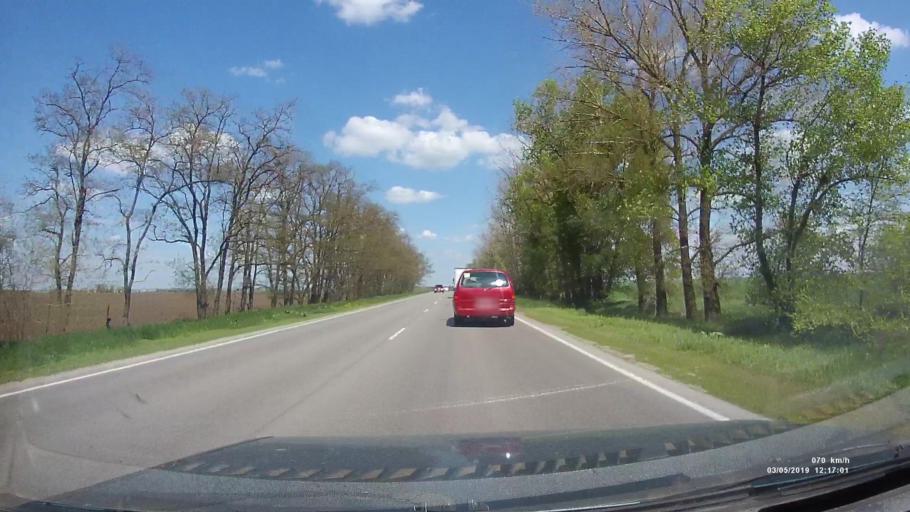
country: RU
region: Rostov
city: Melikhovskaya
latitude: 47.3784
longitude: 40.5891
